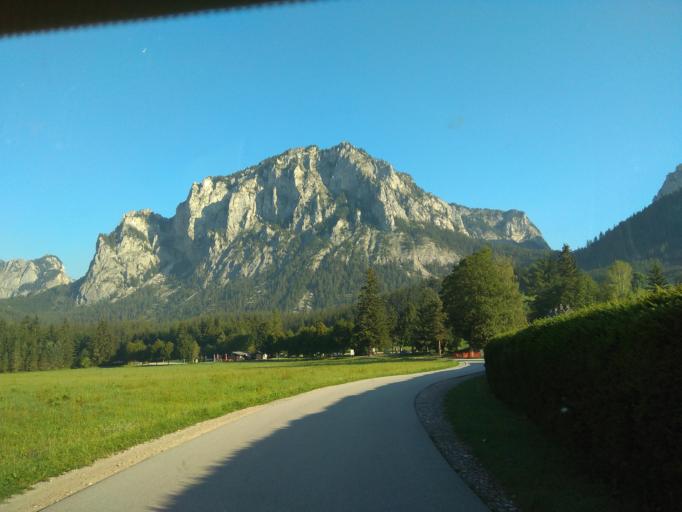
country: AT
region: Styria
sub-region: Politischer Bezirk Leoben
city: Vordernberg
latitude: 47.5350
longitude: 15.0695
